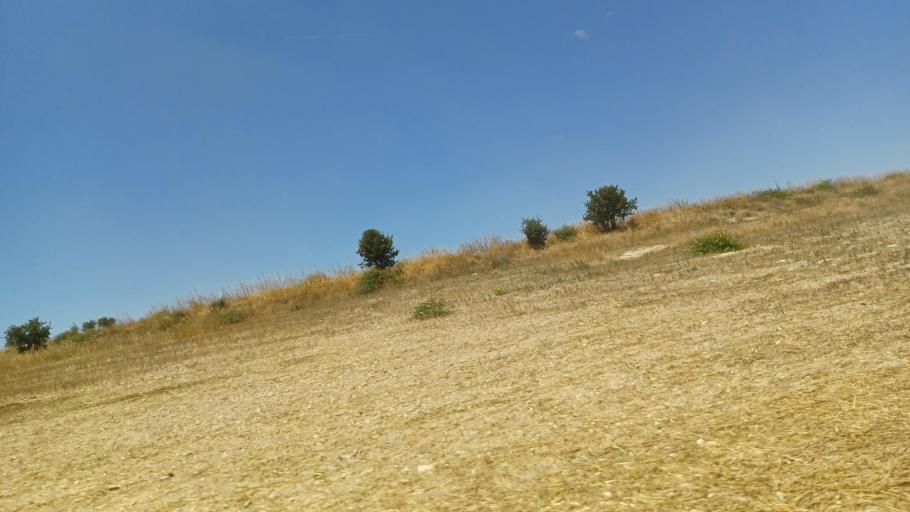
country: CY
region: Lefkosia
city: Lympia
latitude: 34.9923
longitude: 33.4884
